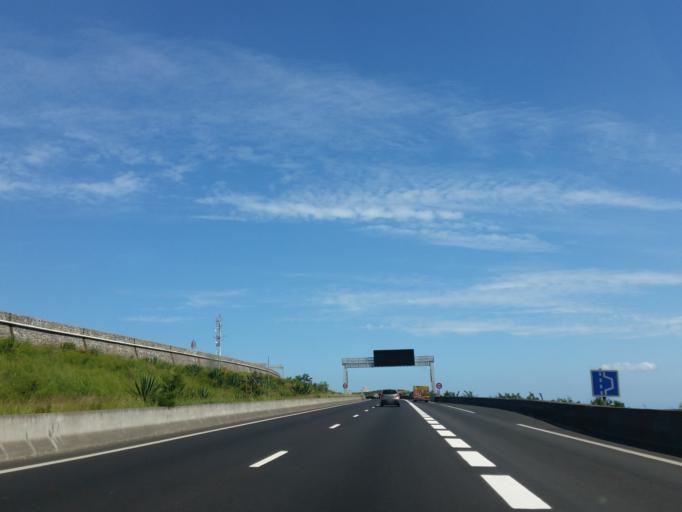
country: RE
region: Reunion
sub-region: Reunion
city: Saint-Paul
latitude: -21.0313
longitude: 55.2525
